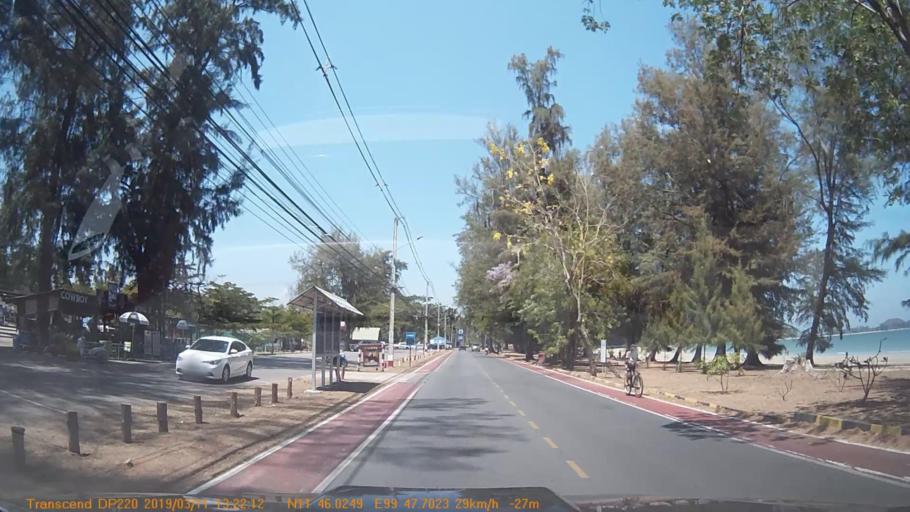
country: TH
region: Prachuap Khiri Khan
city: Prachuap Khiri Khan
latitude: 11.7672
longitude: 99.7950
